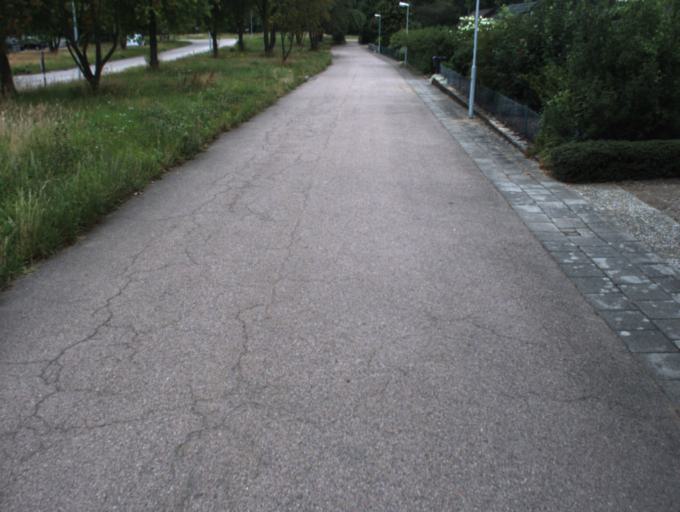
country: SE
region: Skane
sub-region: Helsingborg
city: Odakra
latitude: 56.0711
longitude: 12.7316
